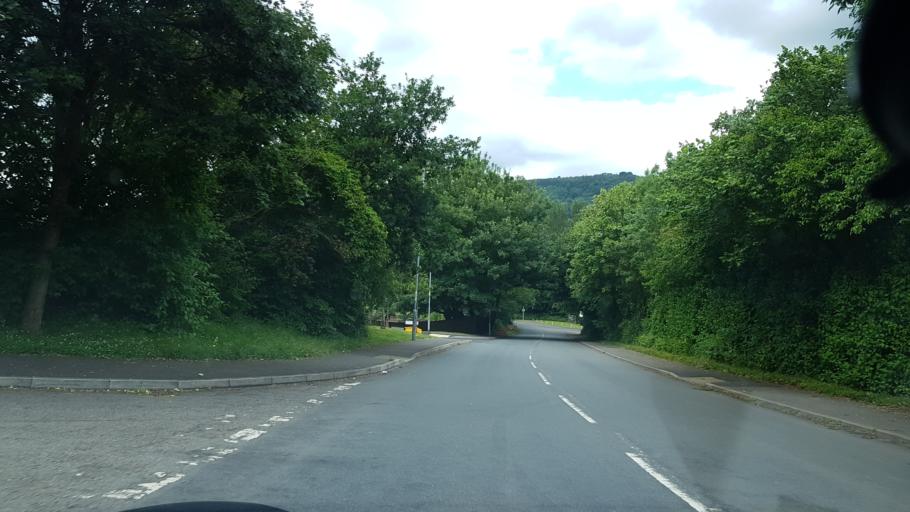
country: GB
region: Wales
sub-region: Monmouthshire
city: Gilwern
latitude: 51.8263
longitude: -3.0820
